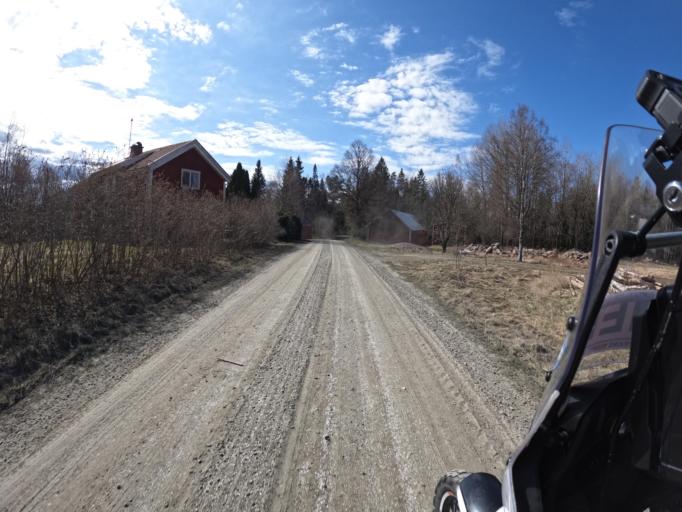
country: SE
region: Vaestra Goetaland
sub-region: Falkopings Kommun
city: Falkoeping
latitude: 57.9539
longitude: 13.6386
